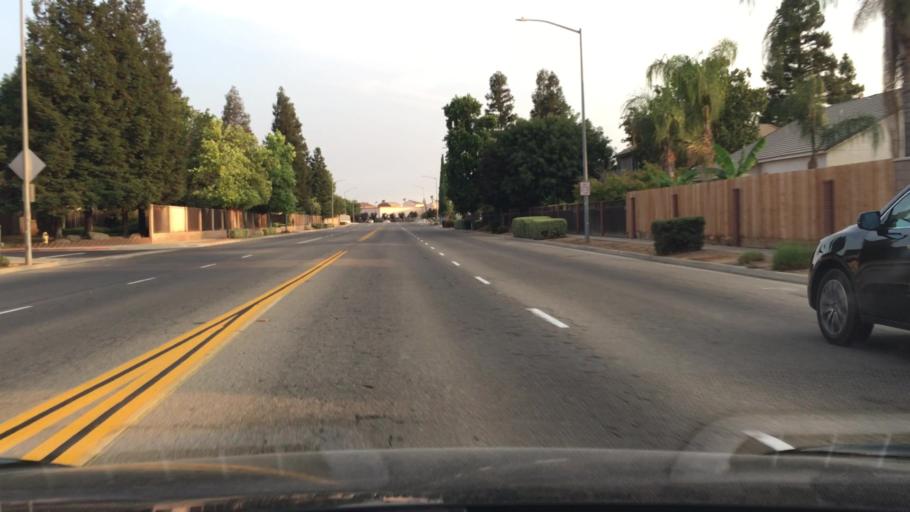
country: US
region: California
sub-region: Fresno County
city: Clovis
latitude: 36.8436
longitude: -119.6930
